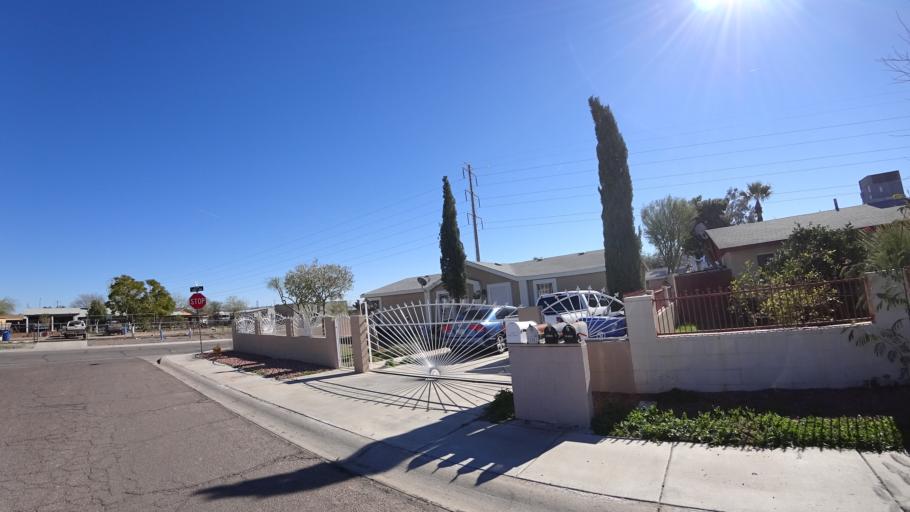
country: US
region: Arizona
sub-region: Maricopa County
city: Avondale
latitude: 33.4127
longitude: -112.3281
